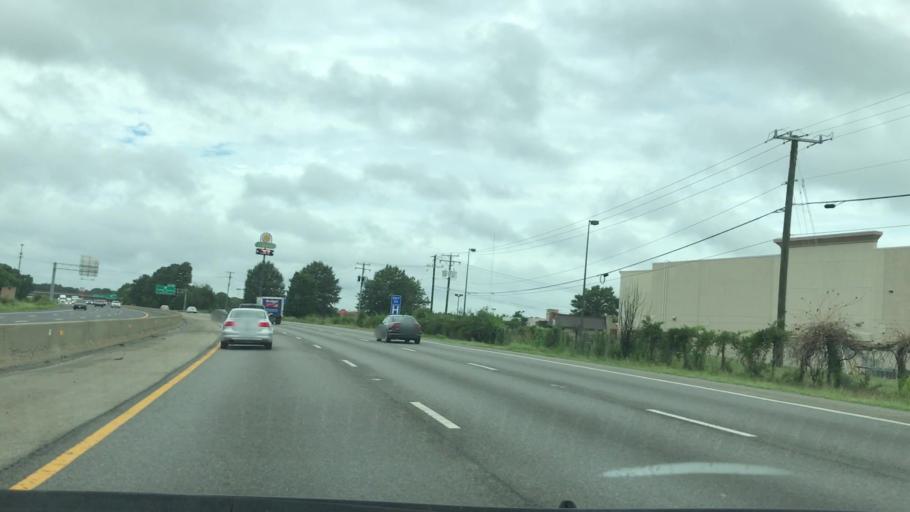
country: US
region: Virginia
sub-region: City of Petersburg
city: Petersburg
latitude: 37.2491
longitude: -77.3934
